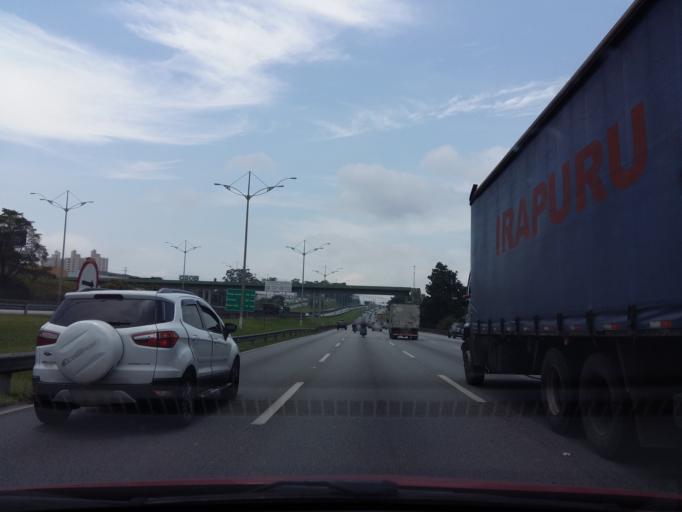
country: BR
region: Sao Paulo
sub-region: Sao Bernardo Do Campo
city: Sao Bernardo do Campo
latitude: -23.6679
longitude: -46.5730
